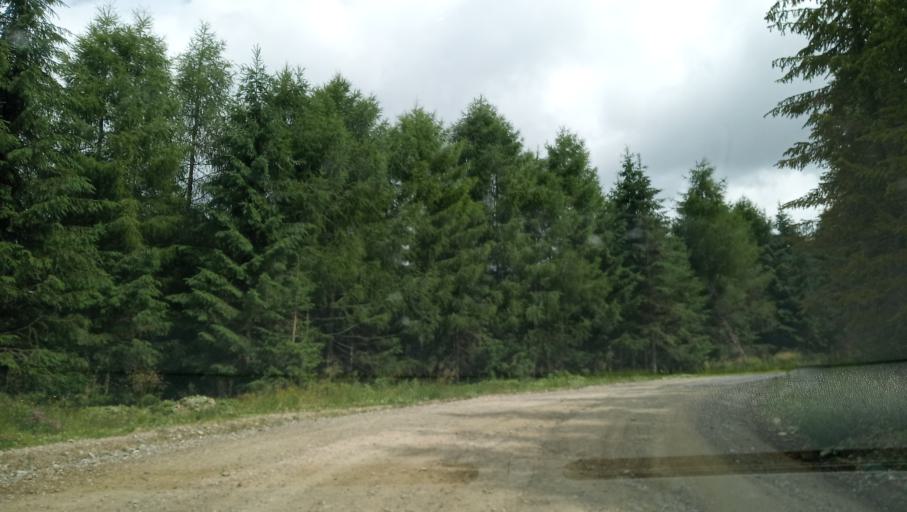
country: RO
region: Hunedoara
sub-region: Oras Petrila
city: Petrila
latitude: 45.4041
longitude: 23.5737
